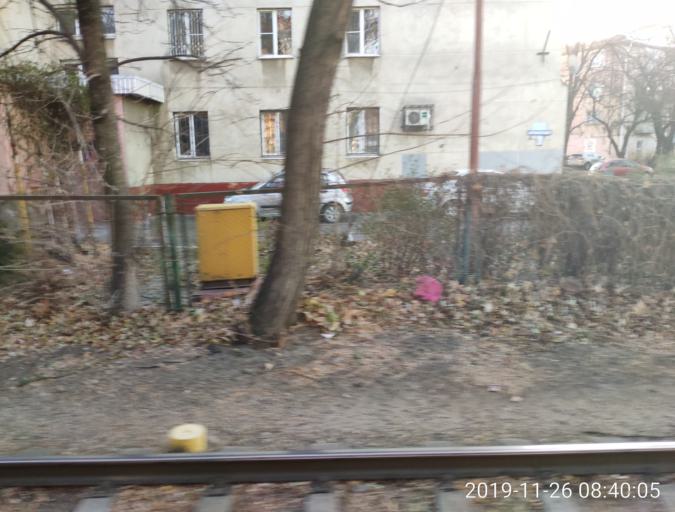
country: RU
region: Krasnodarskiy
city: Krasnodar
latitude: 45.0566
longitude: 38.9847
